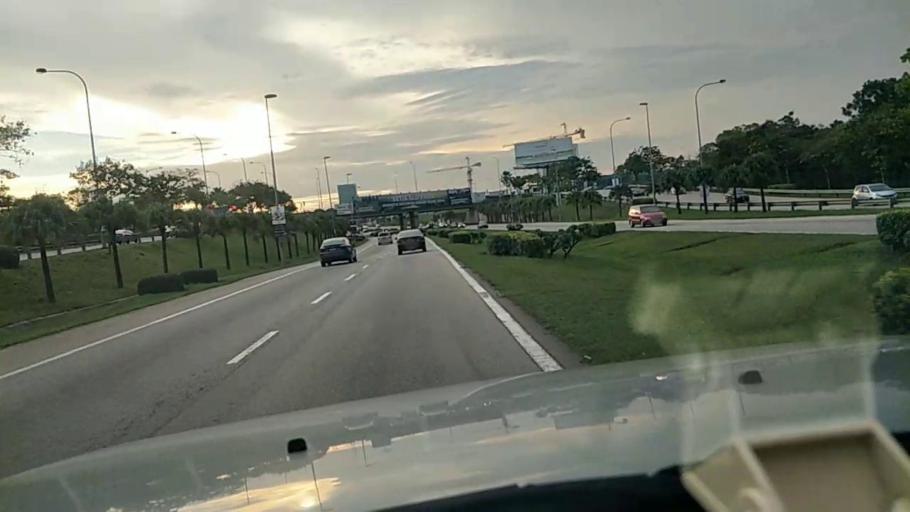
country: MY
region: Selangor
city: Shah Alam
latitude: 3.1035
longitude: 101.4717
